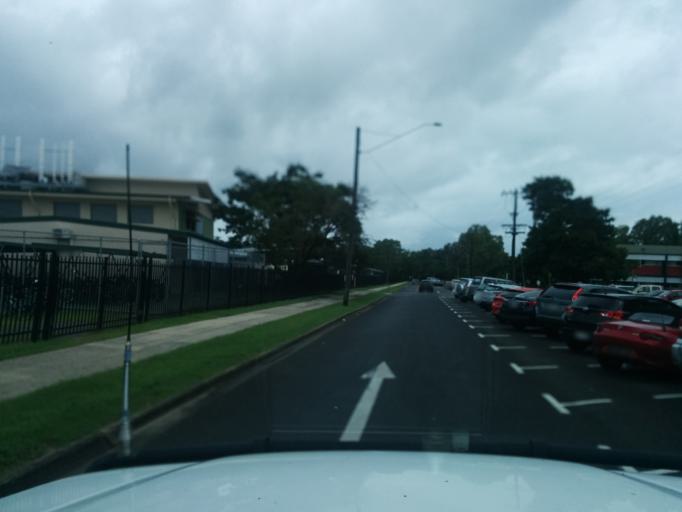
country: AU
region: Queensland
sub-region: Cairns
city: Cairns
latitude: -16.9228
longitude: 145.7535
